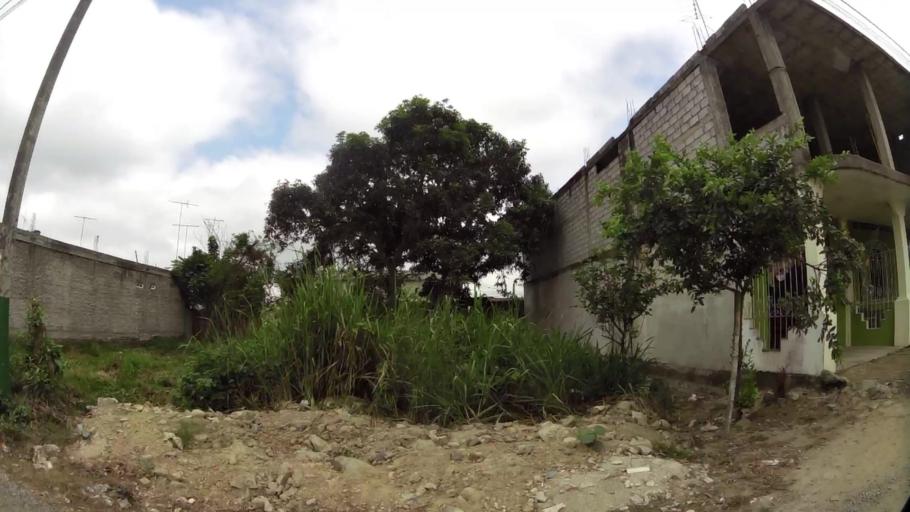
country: EC
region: Guayas
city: Naranjal
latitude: -2.6793
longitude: -79.6252
